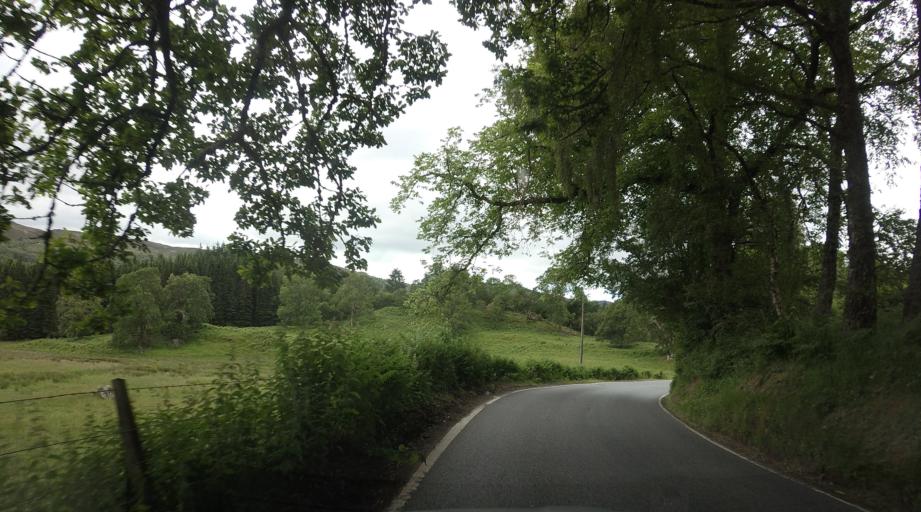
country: GB
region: Scotland
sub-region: Perth and Kinross
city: Pitlochry
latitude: 56.7278
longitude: -3.8215
